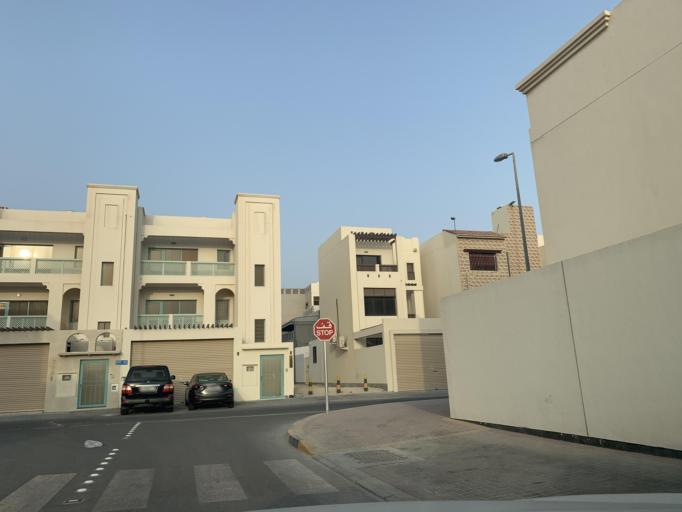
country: BH
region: Manama
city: Jidd Hafs
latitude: 26.2177
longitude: 50.4395
